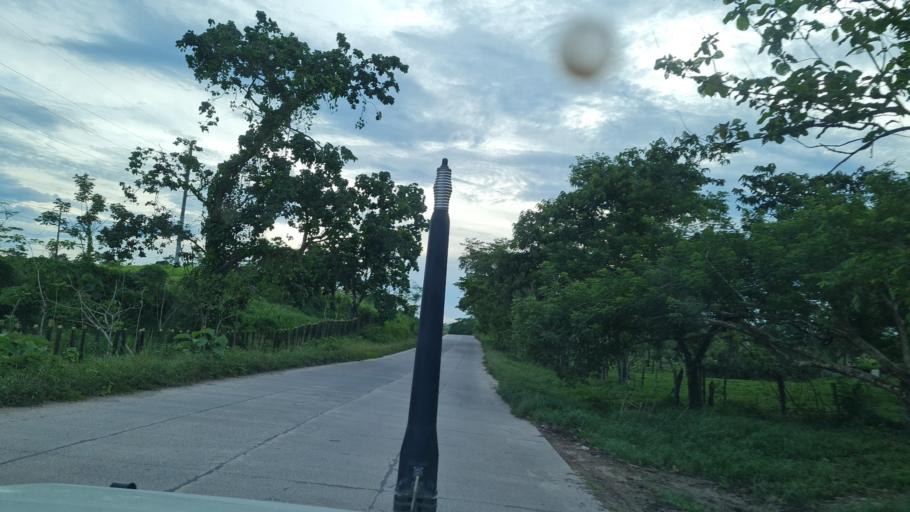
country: NI
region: Atlantico Norte (RAAN)
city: Siuna
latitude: 13.6850
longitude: -84.6017
